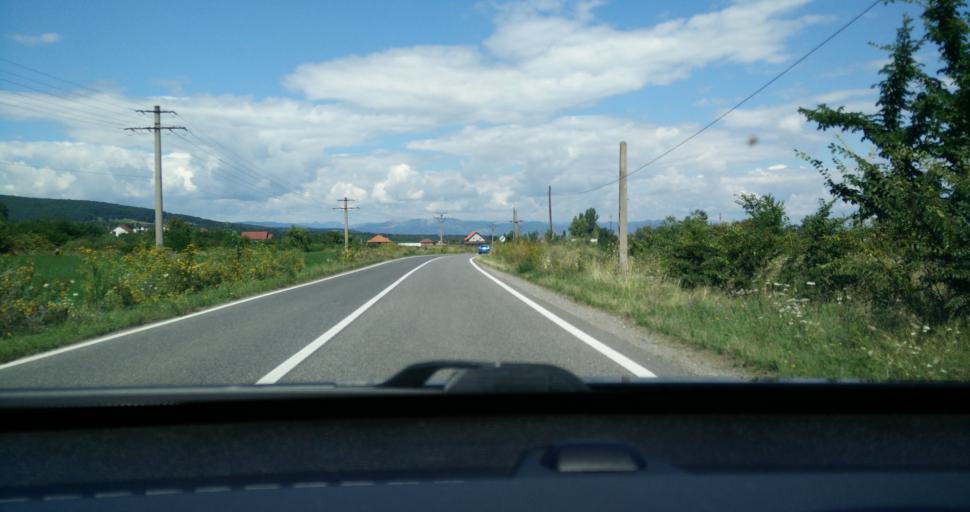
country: RO
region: Alba
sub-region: Comuna Sasciori
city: Sebesel
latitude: 45.9006
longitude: 23.5586
